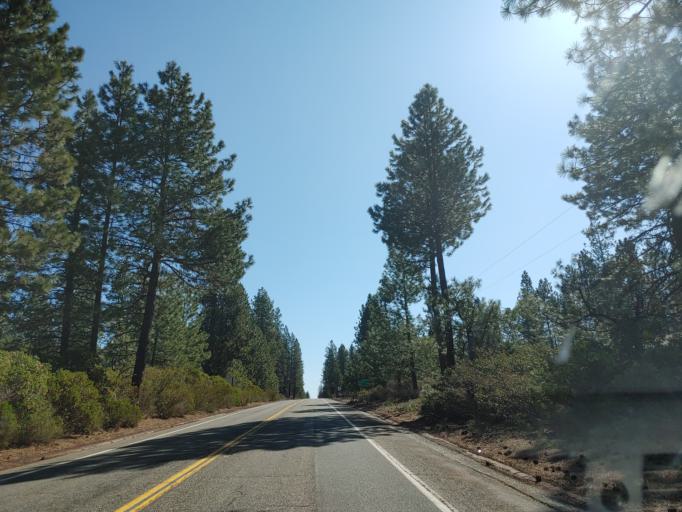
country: US
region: California
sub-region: Siskiyou County
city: McCloud
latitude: 41.2512
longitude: -122.1254
